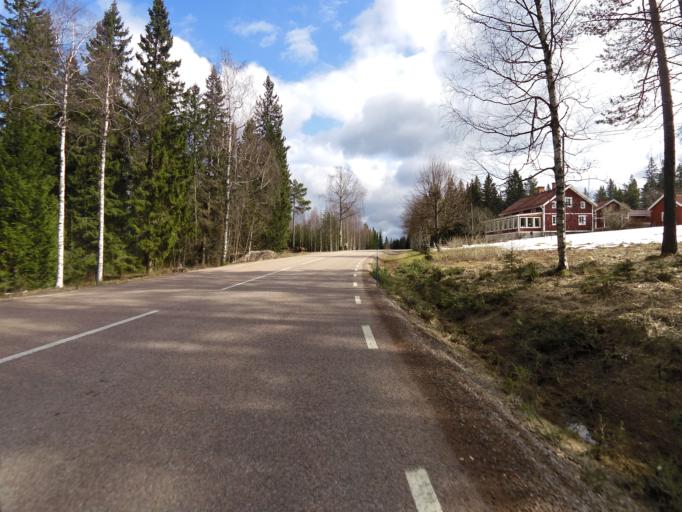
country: SE
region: Dalarna
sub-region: Avesta Kommun
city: Horndal
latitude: 60.2951
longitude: 16.2859
